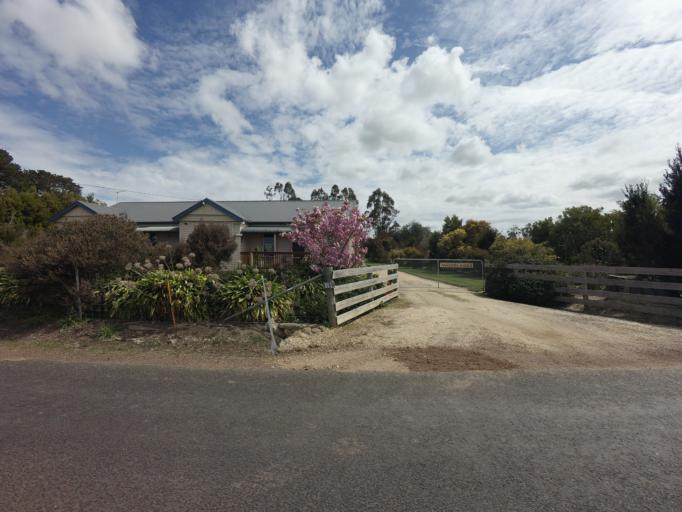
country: AU
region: Tasmania
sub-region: Northern Midlands
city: Longford
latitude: -41.6863
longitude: 147.1970
